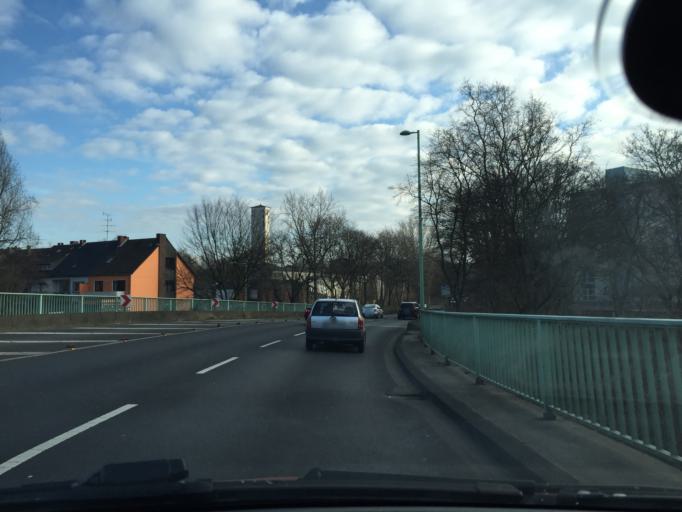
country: DE
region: North Rhine-Westphalia
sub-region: Regierungsbezirk Koln
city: Deutz
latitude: 50.9315
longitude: 6.9748
